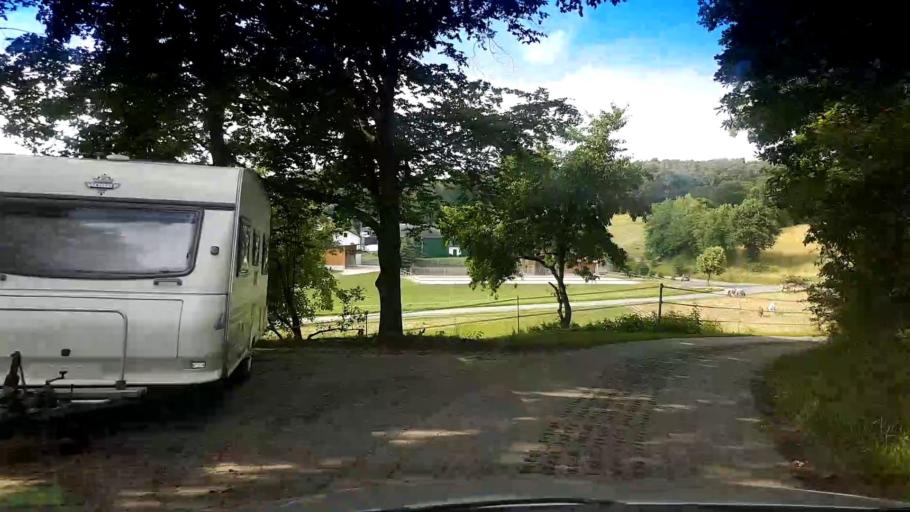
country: DE
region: Bavaria
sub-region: Upper Franconia
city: Walsdorf
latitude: 49.8752
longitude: 10.7990
